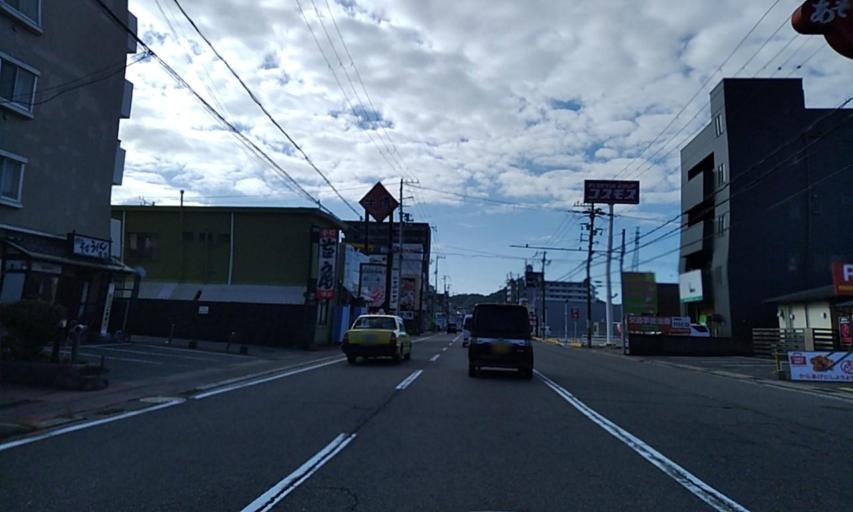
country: JP
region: Wakayama
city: Minato
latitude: 34.2063
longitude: 135.1593
